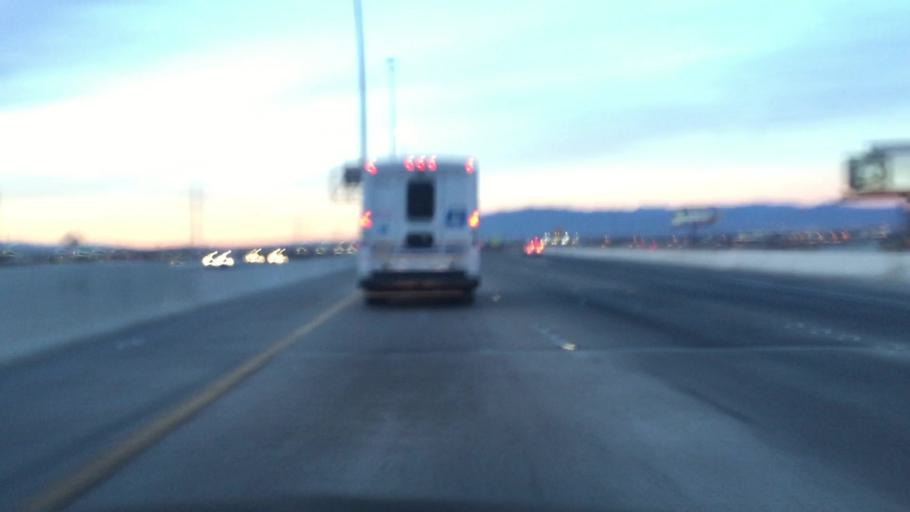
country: US
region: Nevada
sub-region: Clark County
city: Henderson
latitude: 36.0593
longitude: -115.0291
